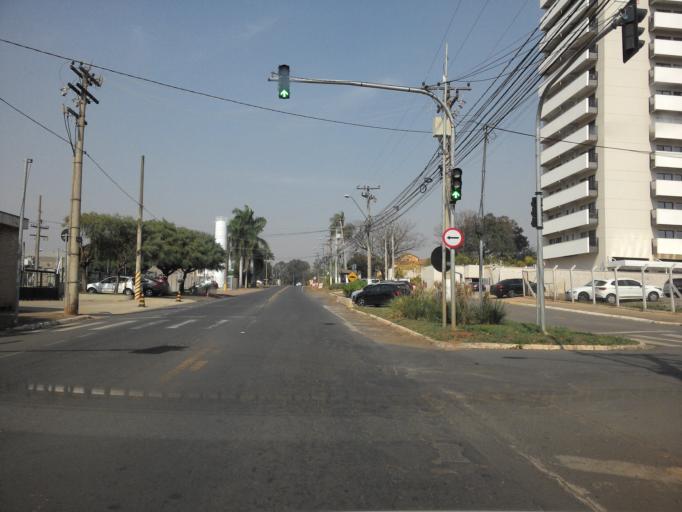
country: BR
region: Sao Paulo
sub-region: Sumare
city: Sumare
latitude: -22.8364
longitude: -47.2592
